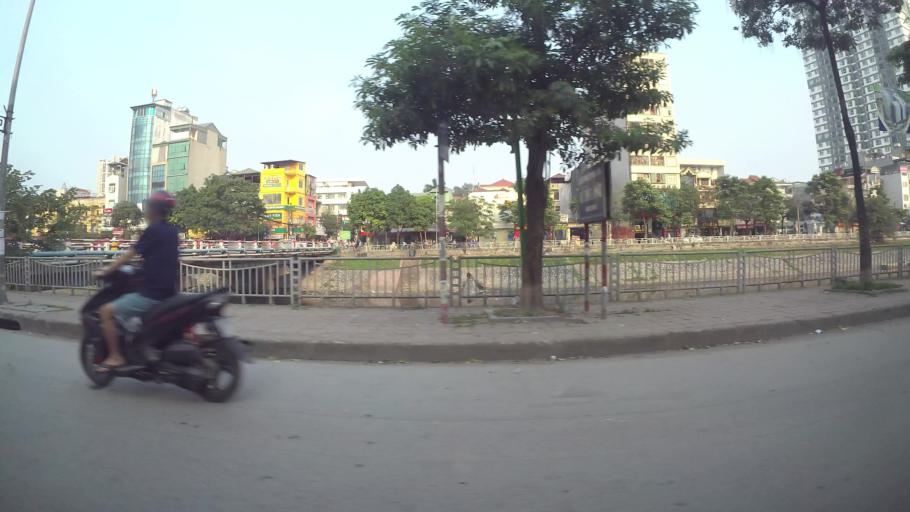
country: VN
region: Ha Noi
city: Thanh Xuan
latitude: 20.9927
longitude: 105.8137
